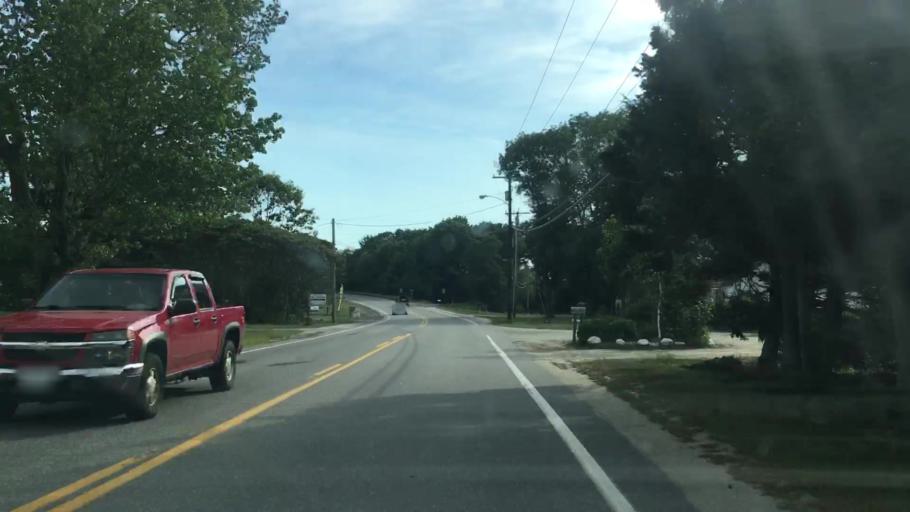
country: US
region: Maine
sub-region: Cumberland County
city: Brunswick
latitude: 43.9153
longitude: -69.9059
